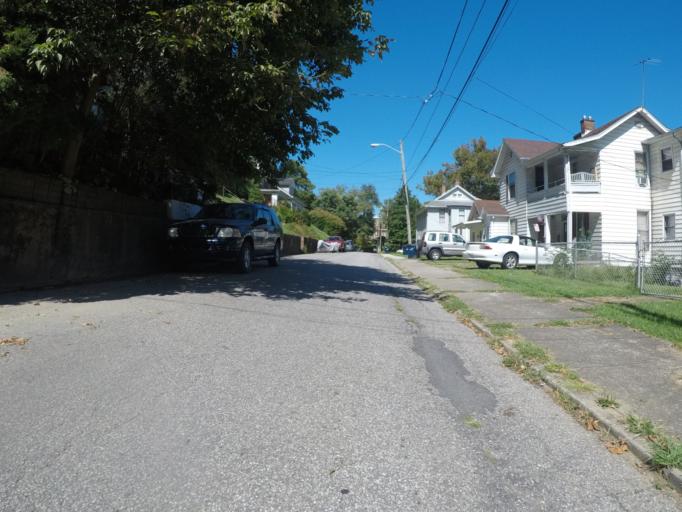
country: US
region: Kentucky
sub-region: Boyd County
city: Ashland
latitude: 38.4729
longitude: -82.6432
